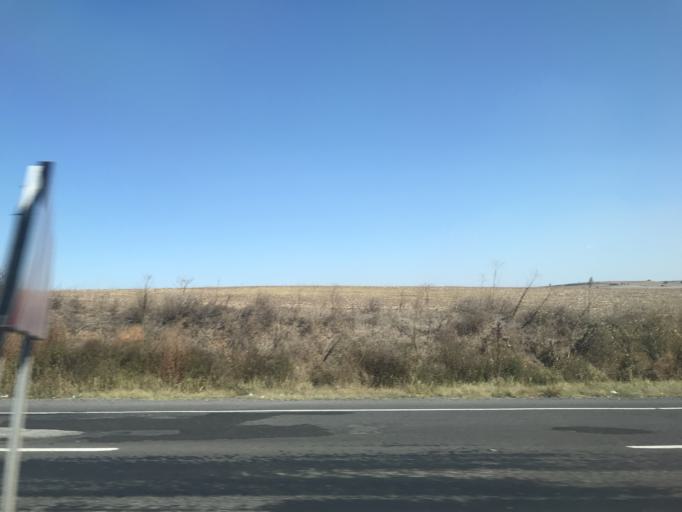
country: TR
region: Tekirdag
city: Muratli
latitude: 41.0917
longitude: 27.4924
